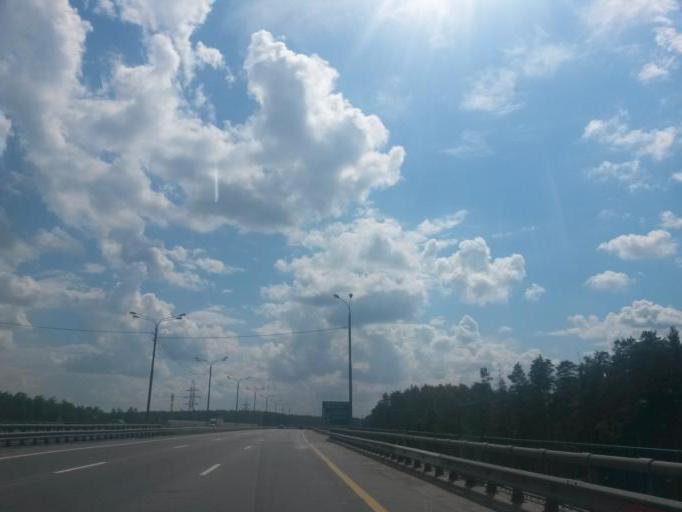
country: RU
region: Moskovskaya
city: Vostryakovo
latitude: 55.4164
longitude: 37.7948
